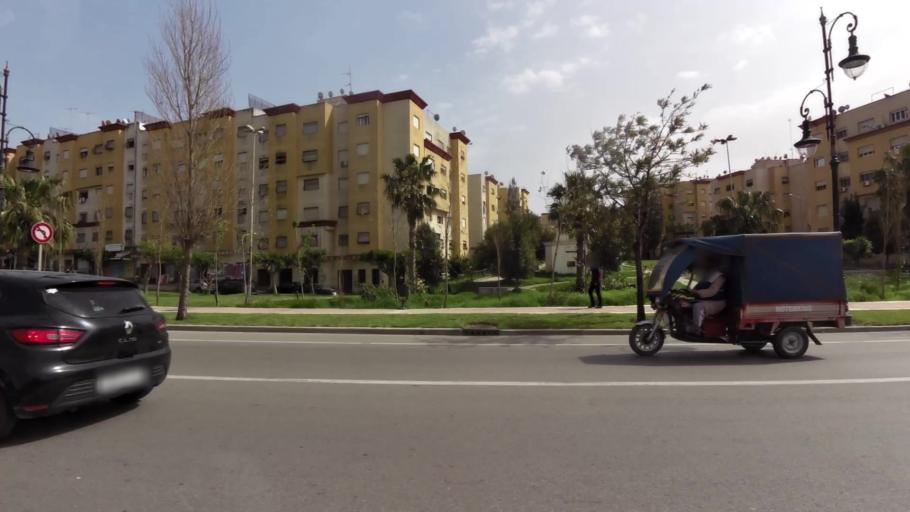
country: MA
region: Tanger-Tetouan
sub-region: Tanger-Assilah
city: Boukhalef
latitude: 35.7372
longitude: -5.8577
